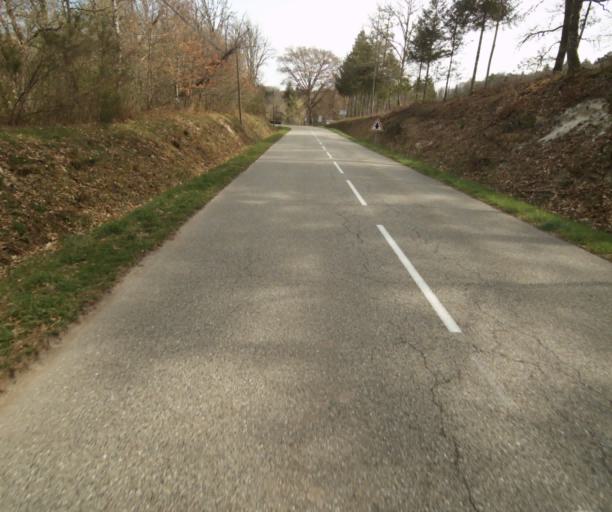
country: FR
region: Limousin
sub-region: Departement de la Correze
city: Correze
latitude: 45.4150
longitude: 1.8304
